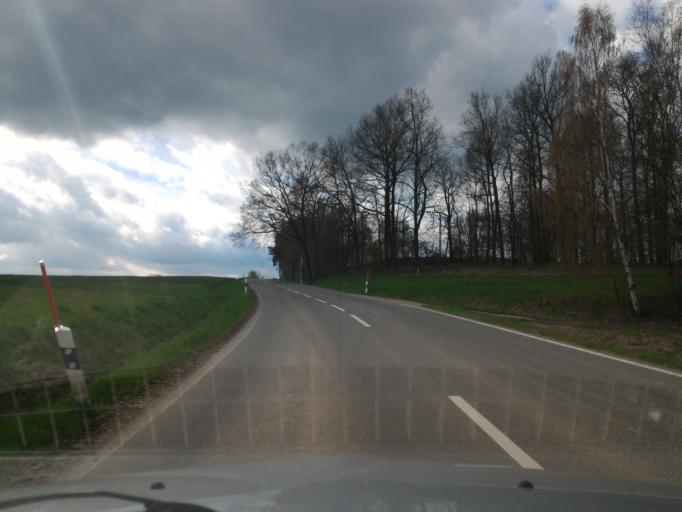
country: DE
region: Saxony
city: Hainewalde
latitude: 50.9239
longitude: 14.7021
